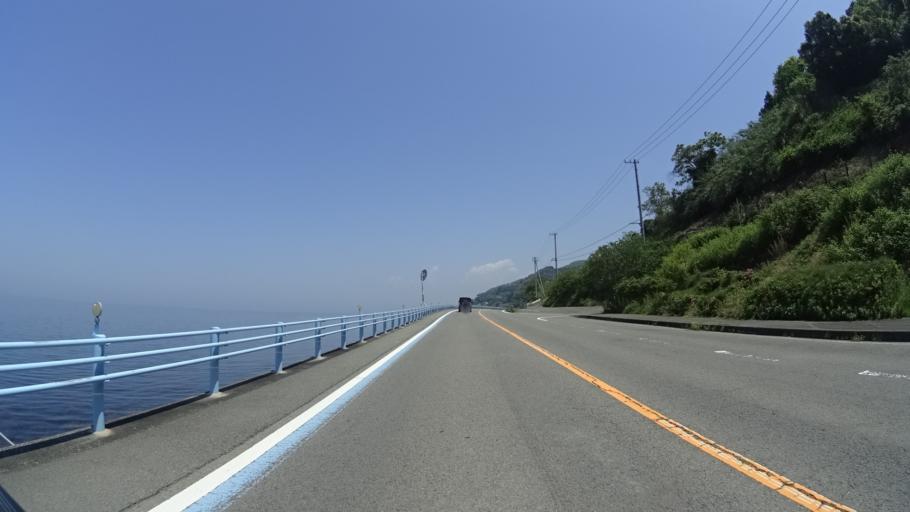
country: JP
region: Ehime
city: Iyo
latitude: 33.6638
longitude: 132.6027
